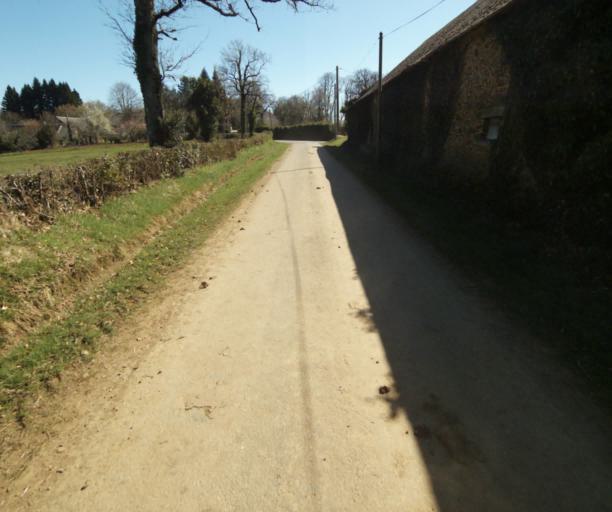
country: FR
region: Limousin
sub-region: Departement de la Correze
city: Seilhac
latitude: 45.3827
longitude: 1.6863
